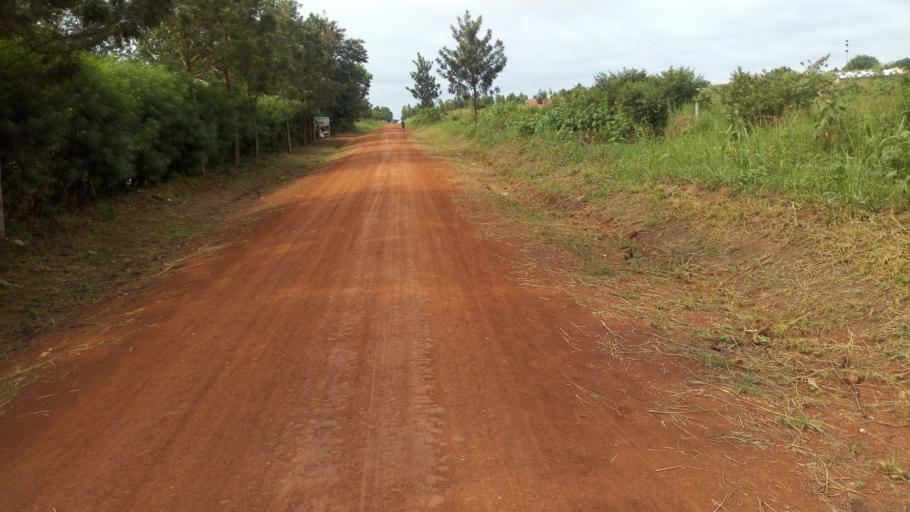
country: UG
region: Western Region
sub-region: Kiryandongo District
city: Kiryandongo
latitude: 1.8036
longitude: 32.0146
